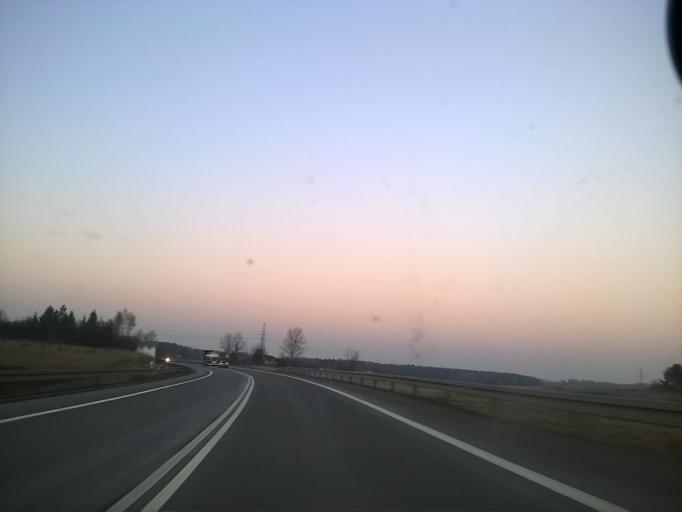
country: PL
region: Warmian-Masurian Voivodeship
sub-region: Powiat olsztynski
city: Barczewo
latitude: 53.7889
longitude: 20.6050
